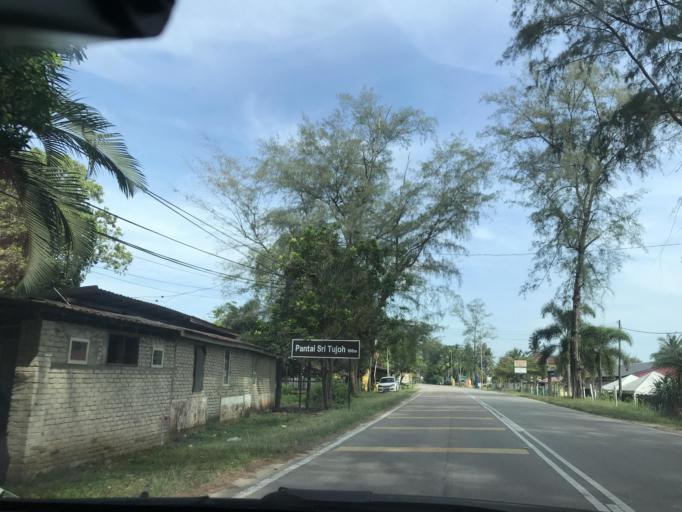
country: MY
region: Kelantan
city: Tumpat
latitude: 6.2142
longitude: 102.1283
